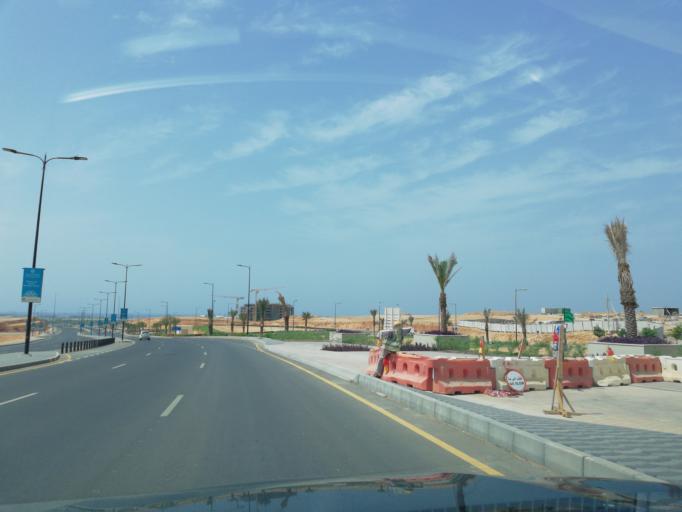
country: OM
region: Muhafazat Masqat
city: Bawshar
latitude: 23.5730
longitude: 58.3253
